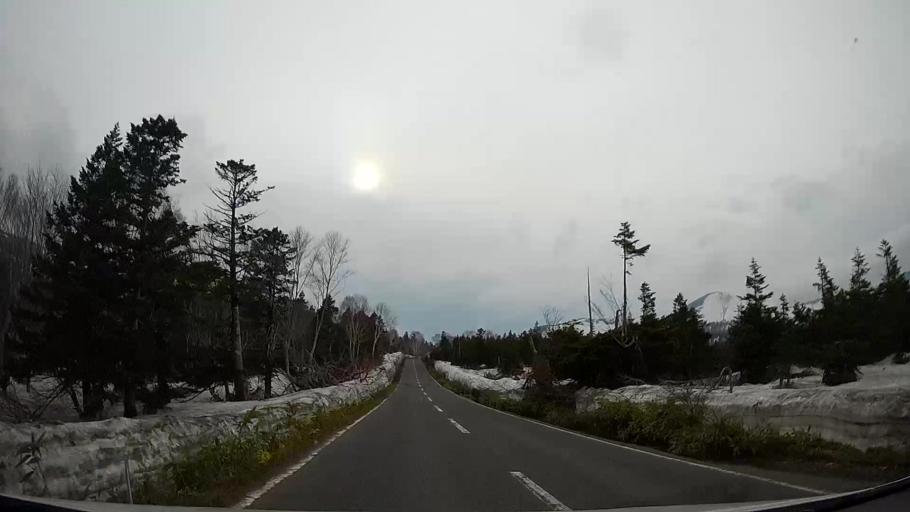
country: JP
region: Aomori
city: Aomori Shi
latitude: 40.6299
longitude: 140.8968
